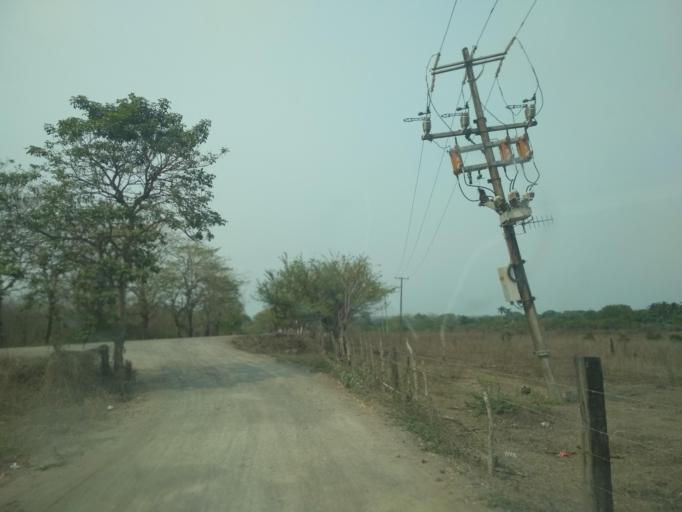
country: MX
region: Veracruz
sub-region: Veracruz
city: Delfino Victoria (Santa Fe)
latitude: 19.1953
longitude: -96.2918
